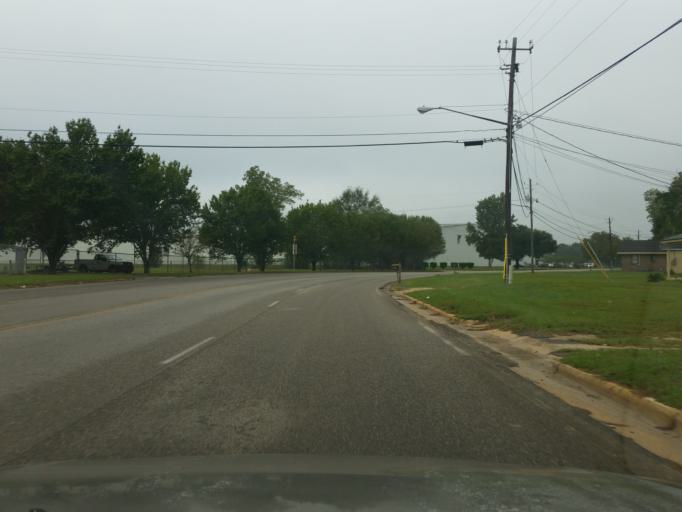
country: US
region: Alabama
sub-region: Baldwin County
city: Bay Minette
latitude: 30.8661
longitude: -87.7841
